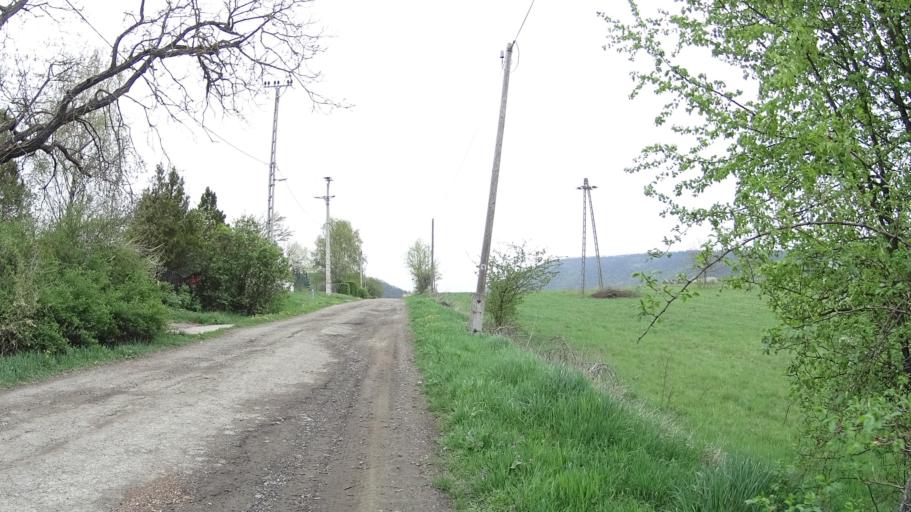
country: HU
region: Pest
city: Kismaros
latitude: 47.8667
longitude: 19.0166
